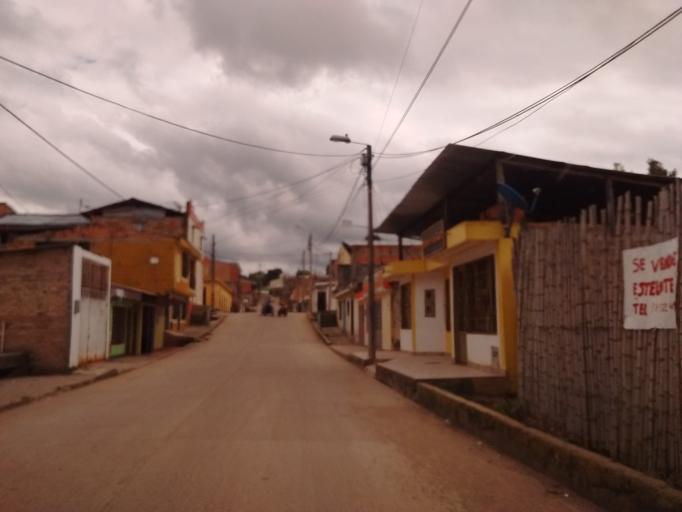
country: CO
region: Huila
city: Isnos
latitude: 1.9309
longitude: -76.2146
